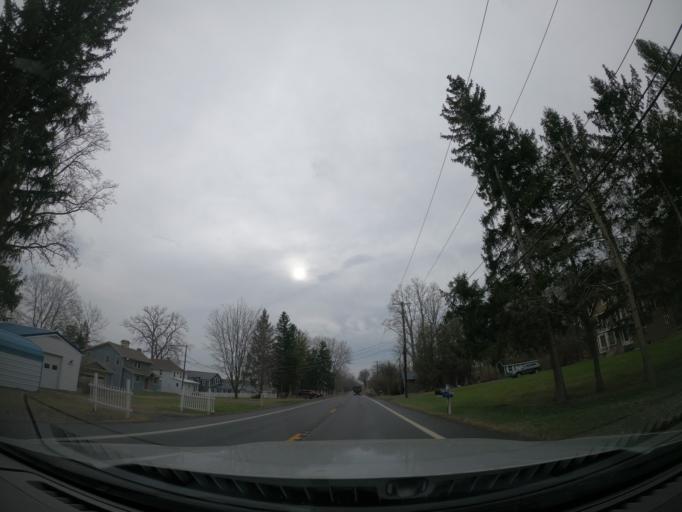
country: US
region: New York
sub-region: Cayuga County
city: Melrose Park
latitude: 42.8457
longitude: -76.5282
